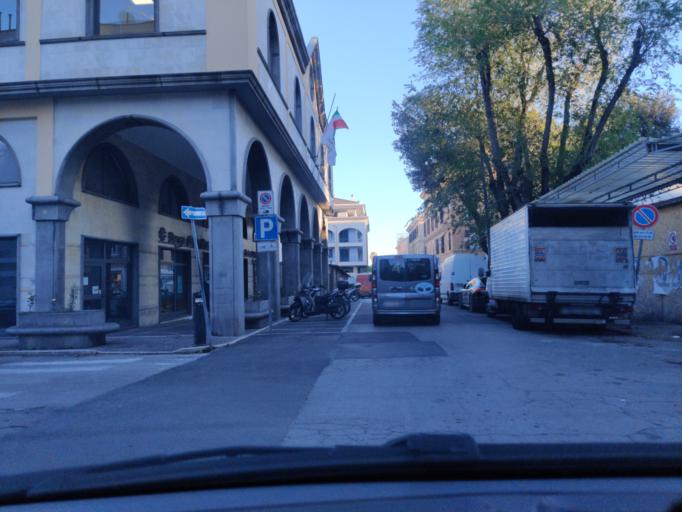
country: IT
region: Latium
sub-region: Citta metropolitana di Roma Capitale
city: Civitavecchia
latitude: 42.0937
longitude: 11.7942
